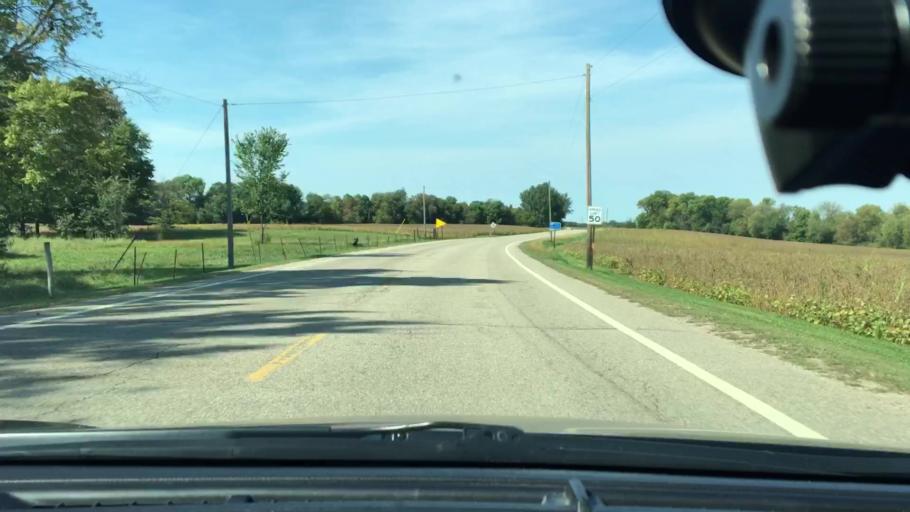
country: US
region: Minnesota
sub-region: Hennepin County
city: Corcoran
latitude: 45.1143
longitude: -93.5852
